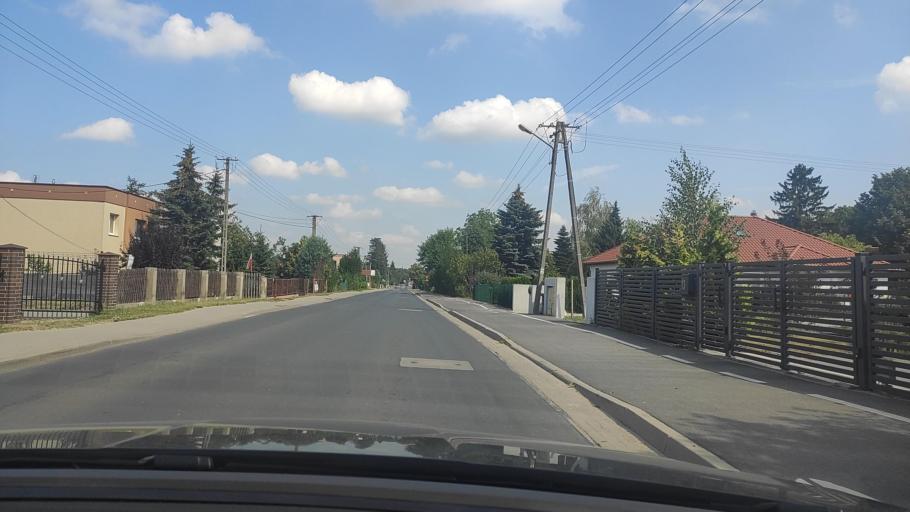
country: PL
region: Greater Poland Voivodeship
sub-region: Powiat poznanski
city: Kostrzyn
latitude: 52.4637
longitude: 17.1693
